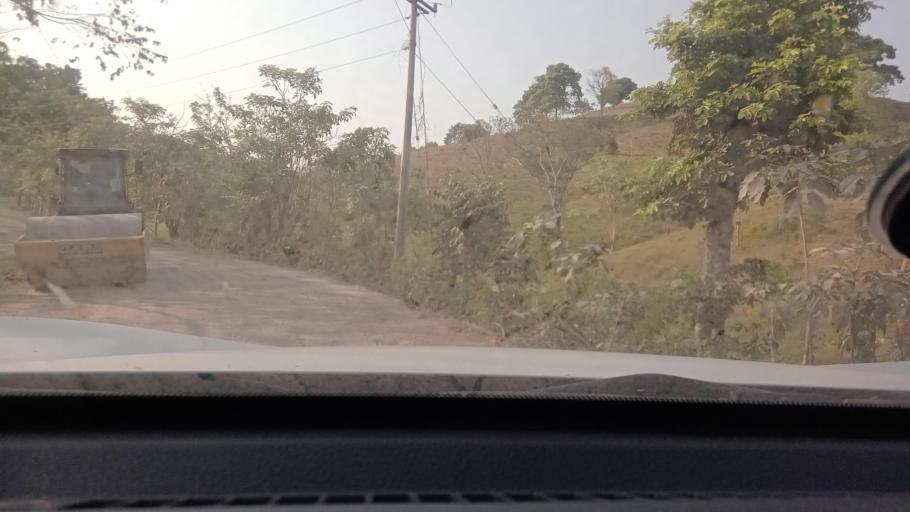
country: MX
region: Tabasco
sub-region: Huimanguillo
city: Francisco Rueda
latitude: 17.6606
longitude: -93.8614
